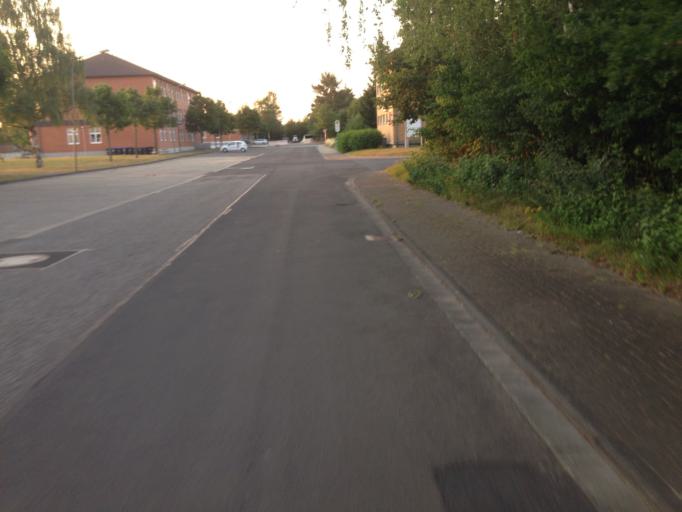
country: DE
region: Hesse
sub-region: Regierungsbezirk Giessen
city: Alten Buseck
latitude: 50.5740
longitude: 8.7286
